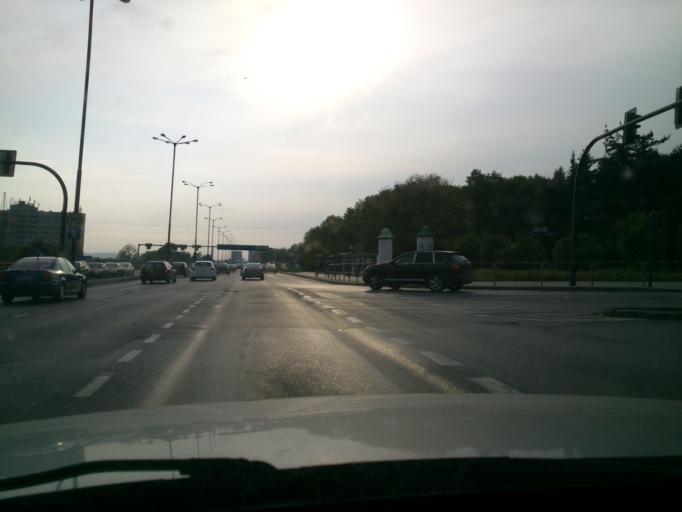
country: PL
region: Lesser Poland Voivodeship
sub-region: Krakow
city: Krakow
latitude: 50.0878
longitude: 20.0017
